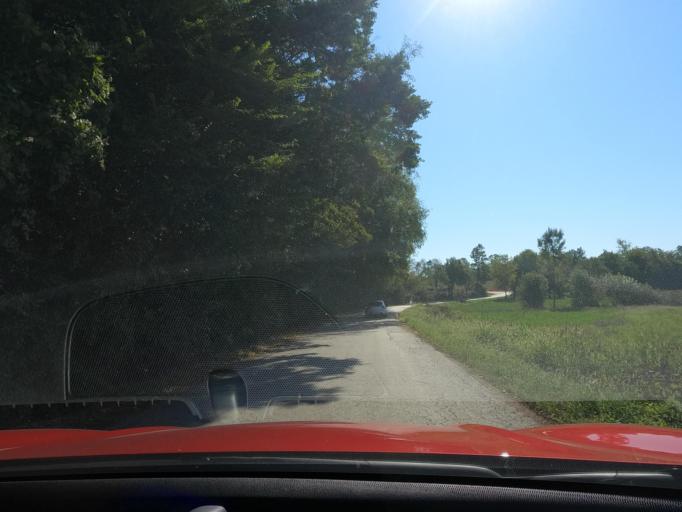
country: RS
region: Central Serbia
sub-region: Raski Okrug
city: Kraljevo
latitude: 43.7754
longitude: 20.6540
